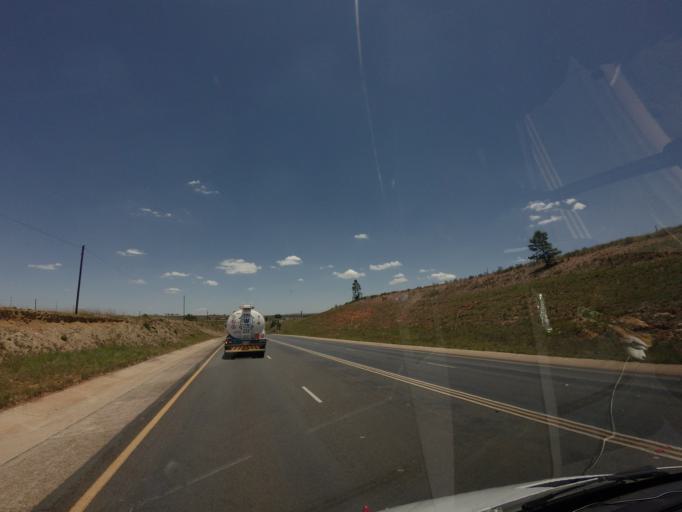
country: ZA
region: Mpumalanga
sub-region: Nkangala District Municipality
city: Belfast
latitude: -25.6610
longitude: 30.2427
